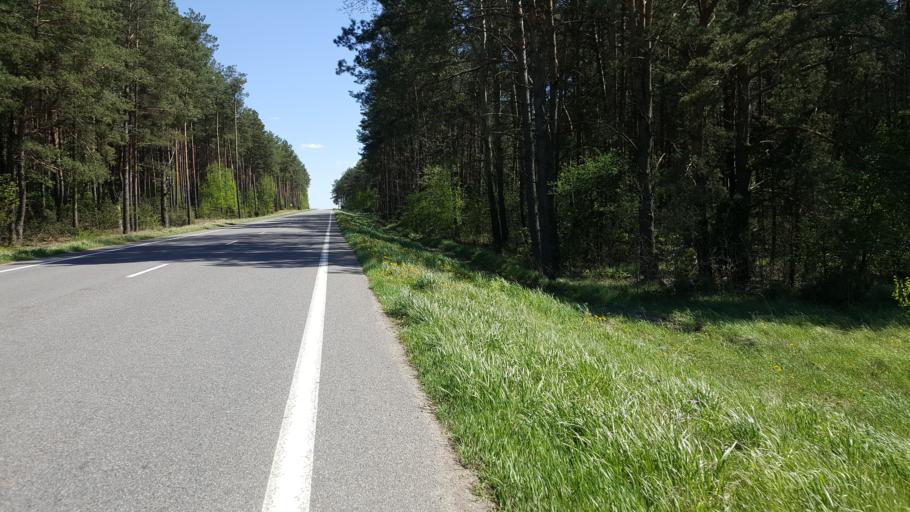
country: BY
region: Brest
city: Kamyanyets
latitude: 52.4782
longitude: 23.8076
